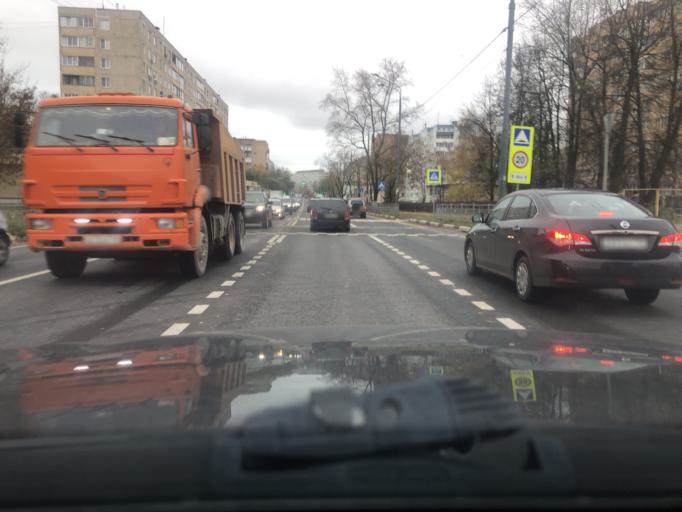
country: RU
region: Moskovskaya
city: Sergiyev Posad
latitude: 56.3275
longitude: 38.1322
